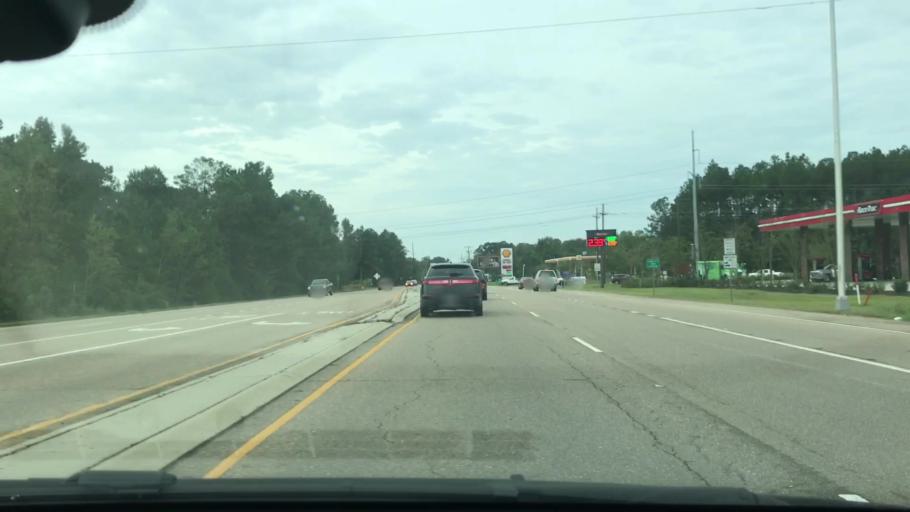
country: US
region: Louisiana
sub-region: Saint Tammany Parish
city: Slidell
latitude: 30.3076
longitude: -89.7718
